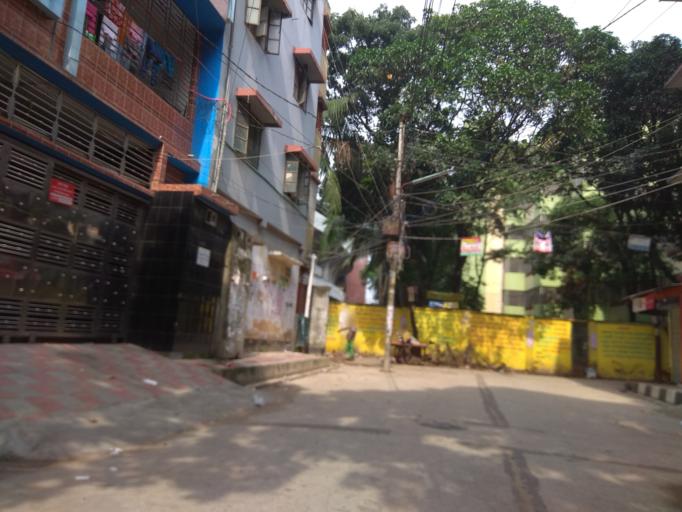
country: BD
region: Dhaka
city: Azimpur
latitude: 23.8082
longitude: 90.3644
